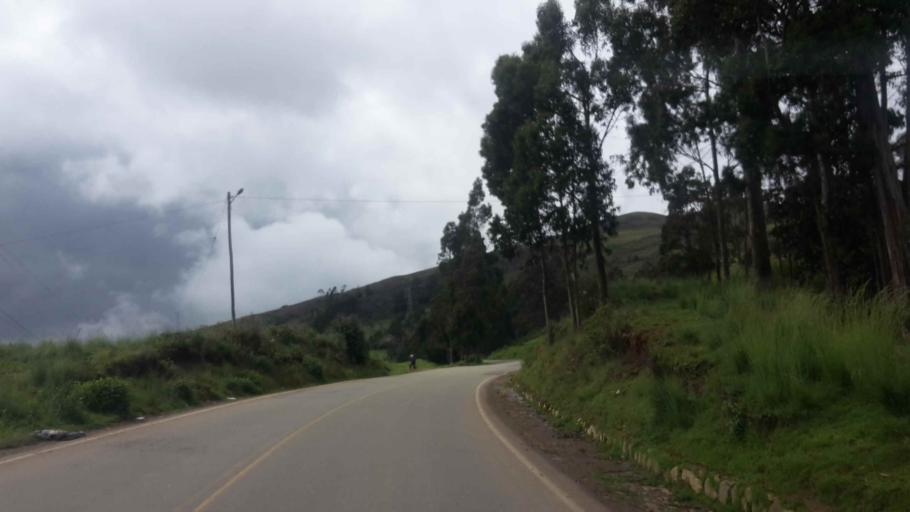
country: BO
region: Cochabamba
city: Totora
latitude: -17.5658
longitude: -65.3343
